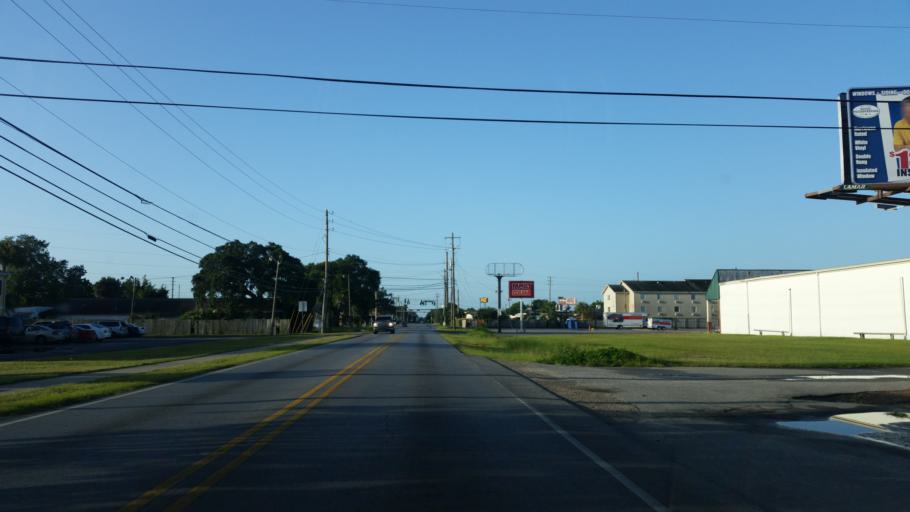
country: US
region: Florida
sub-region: Escambia County
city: West Pensacola
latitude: 30.4092
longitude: -87.2748
